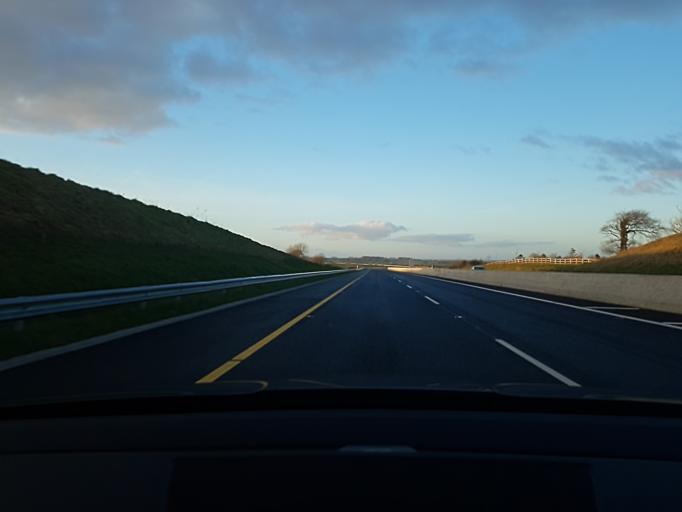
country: IE
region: Connaught
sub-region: County Galway
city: Tuam
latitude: 53.4116
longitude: -8.8273
